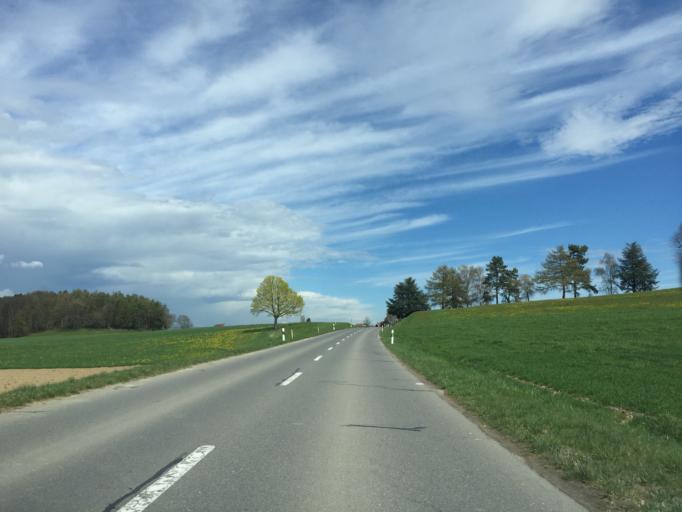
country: CH
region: Vaud
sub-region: Morges District
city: Grancy
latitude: 46.5861
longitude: 6.4588
